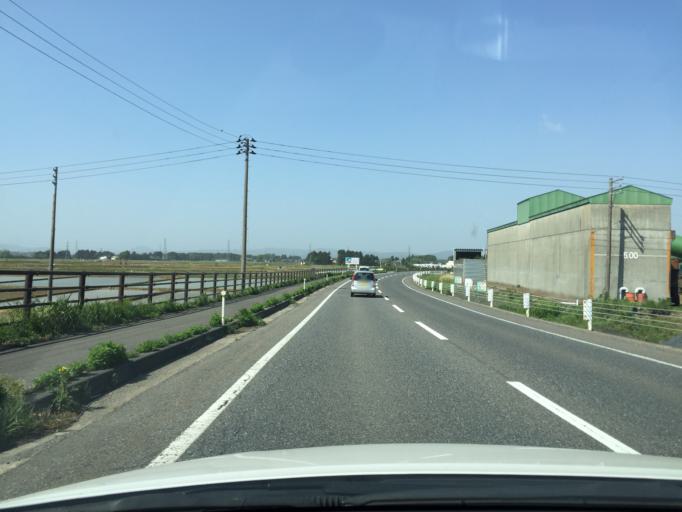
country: JP
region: Niigata
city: Gosen
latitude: 37.7490
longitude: 139.2172
